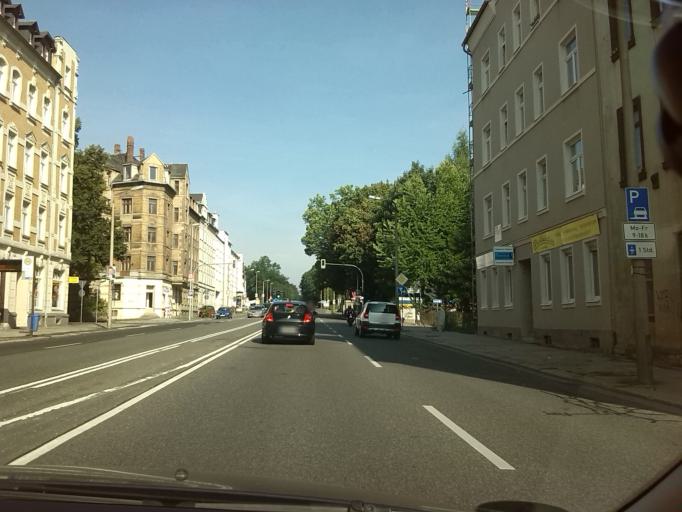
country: DE
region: Saxony
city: Chemnitz
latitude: 50.8458
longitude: 12.9036
